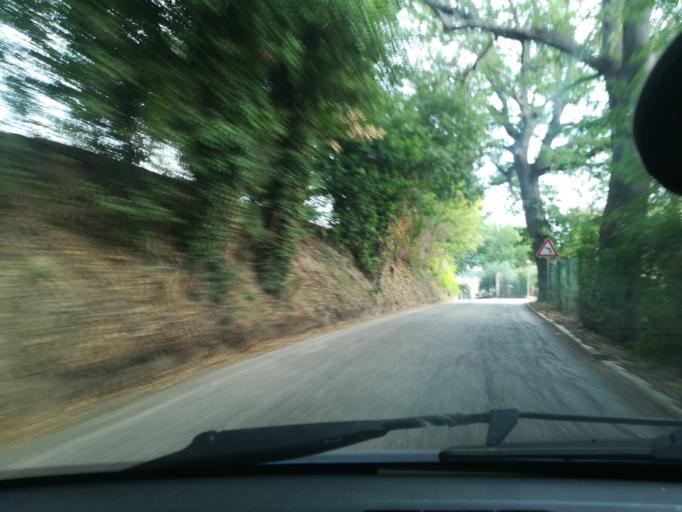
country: IT
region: The Marches
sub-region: Provincia di Macerata
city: Piediripa
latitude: 43.2952
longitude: 13.4845
